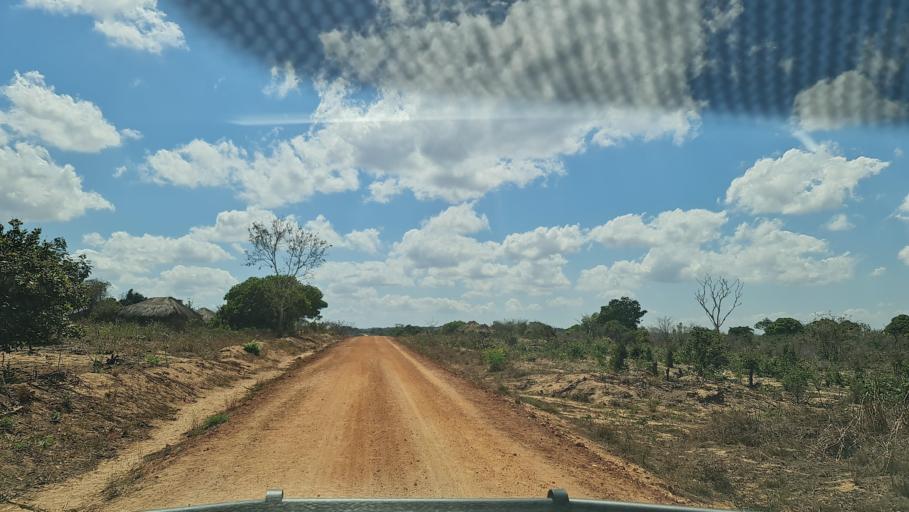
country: MZ
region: Nampula
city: Nacala
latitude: -14.1761
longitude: 40.2304
